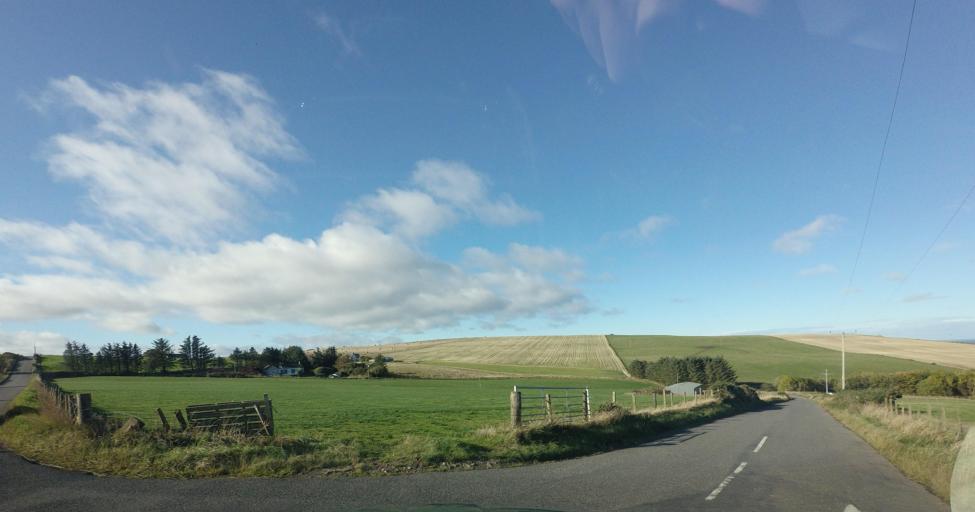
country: GB
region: Scotland
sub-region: Aberdeenshire
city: Macduff
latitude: 57.6622
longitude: -2.3196
